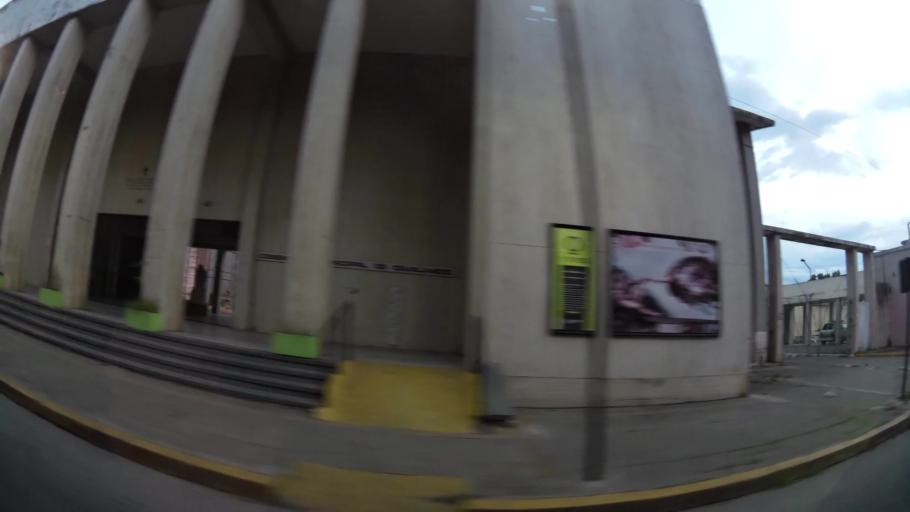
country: AR
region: Buenos Aires
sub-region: Partido de Quilmes
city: Quilmes
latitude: -34.7434
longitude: -58.2281
